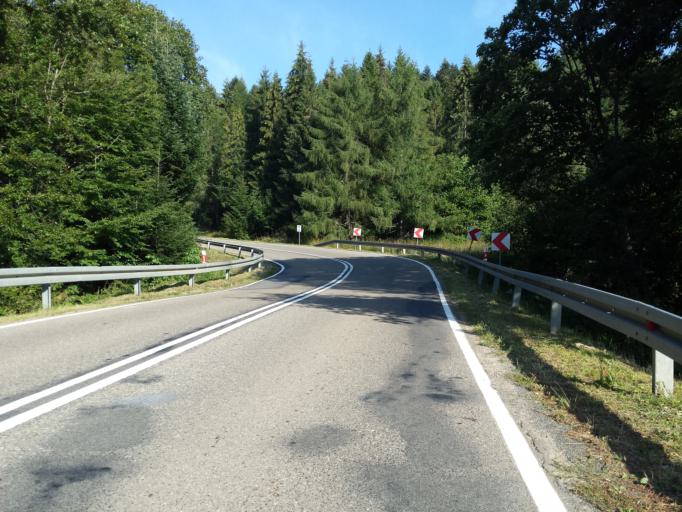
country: PL
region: Subcarpathian Voivodeship
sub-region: Powiat leski
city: Cisna
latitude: 49.2362
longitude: 22.3008
